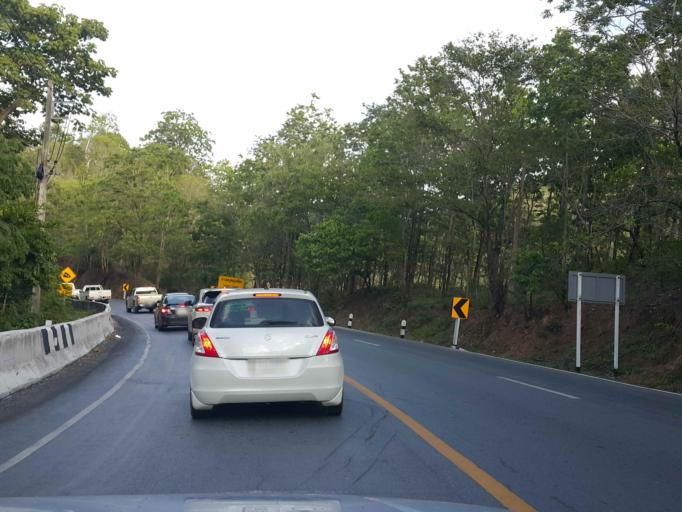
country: TH
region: Tak
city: Tak
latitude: 16.8135
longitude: 98.9719
